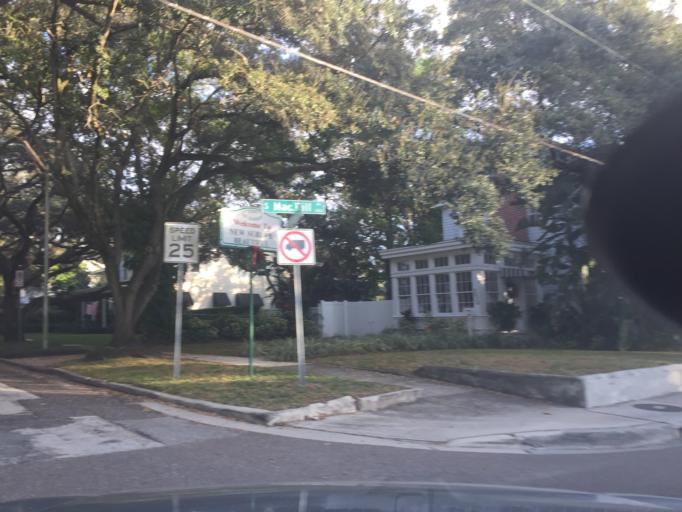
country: US
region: Florida
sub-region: Hillsborough County
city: Tampa
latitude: 27.9306
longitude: -82.4934
